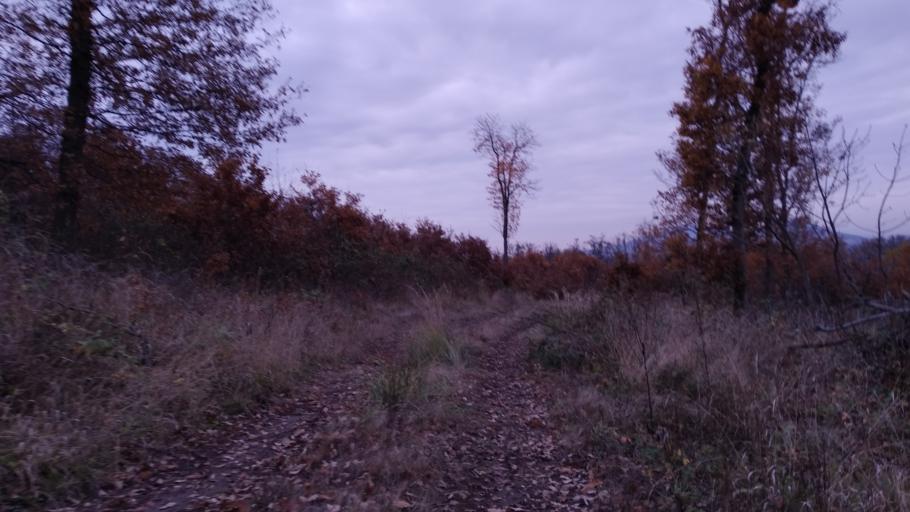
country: HU
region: Pest
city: Csobanka
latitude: 47.6756
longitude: 18.9592
